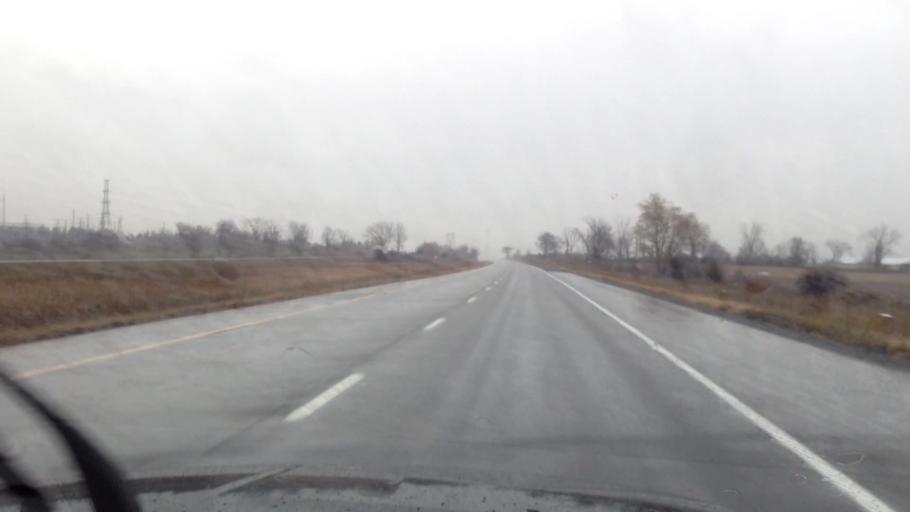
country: CA
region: Ontario
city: Casselman
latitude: 45.3701
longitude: -74.8542
